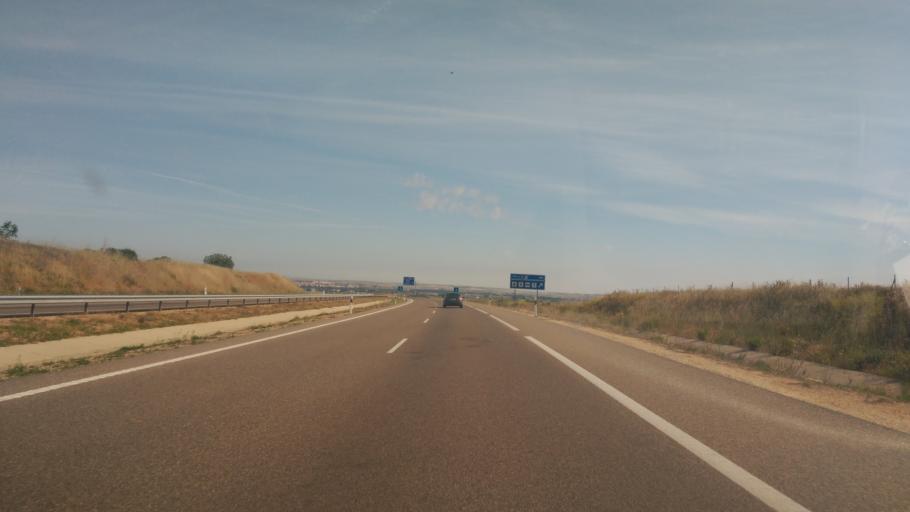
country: ES
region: Castille and Leon
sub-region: Provincia de Zamora
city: Morales del Vino
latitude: 41.4415
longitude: -5.7180
